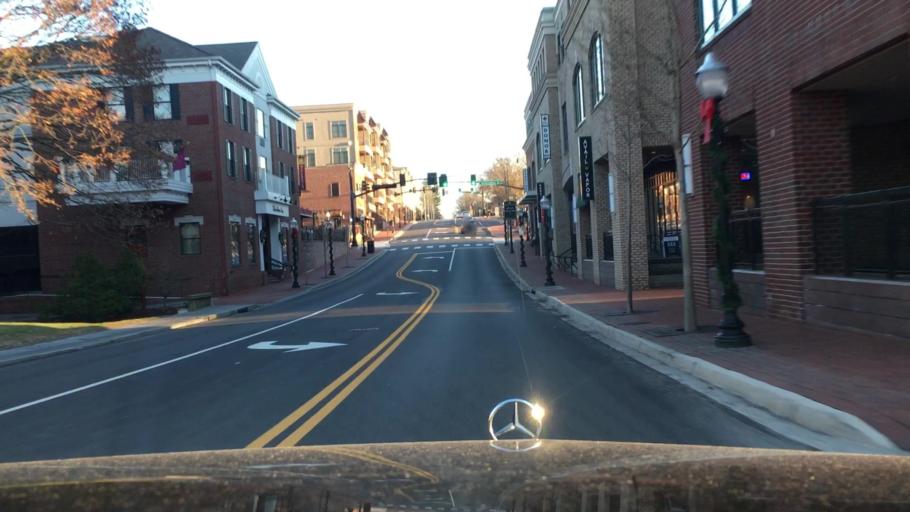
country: US
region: Virginia
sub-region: Montgomery County
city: Blacksburg
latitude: 37.2286
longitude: -80.4132
